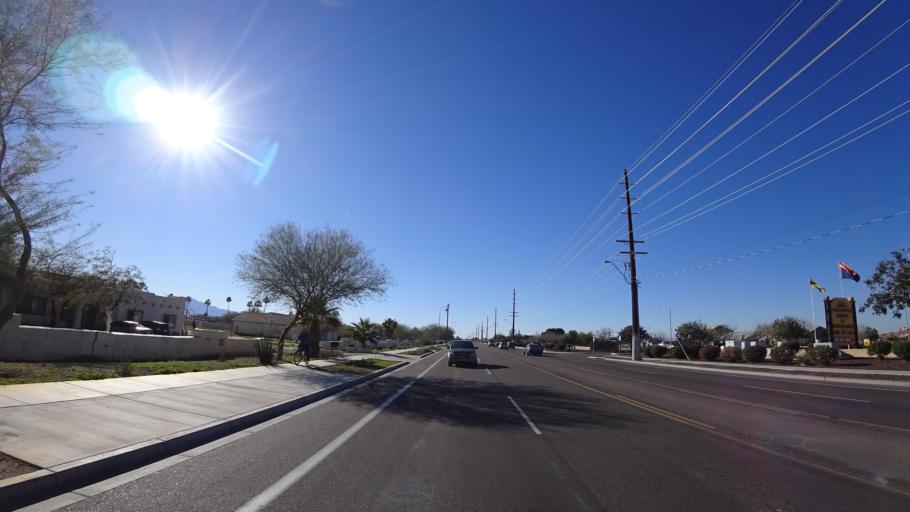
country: US
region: Arizona
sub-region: Maricopa County
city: Laveen
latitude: 33.3921
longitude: -112.1186
